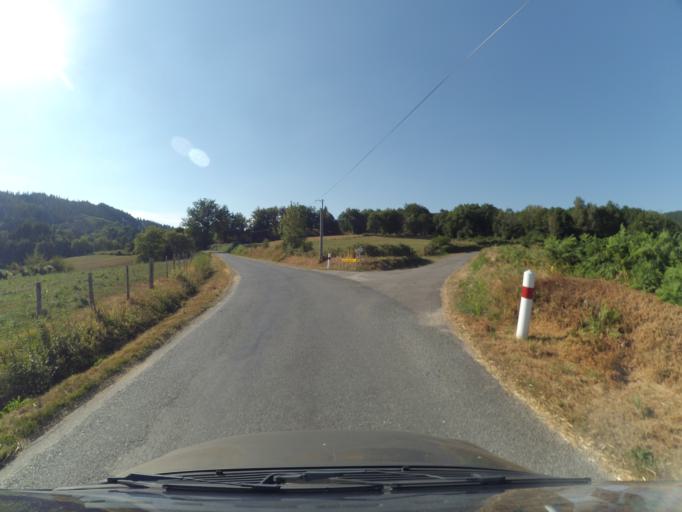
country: FR
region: Limousin
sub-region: Departement de la Haute-Vienne
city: Eymoutiers
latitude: 45.7523
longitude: 1.8197
